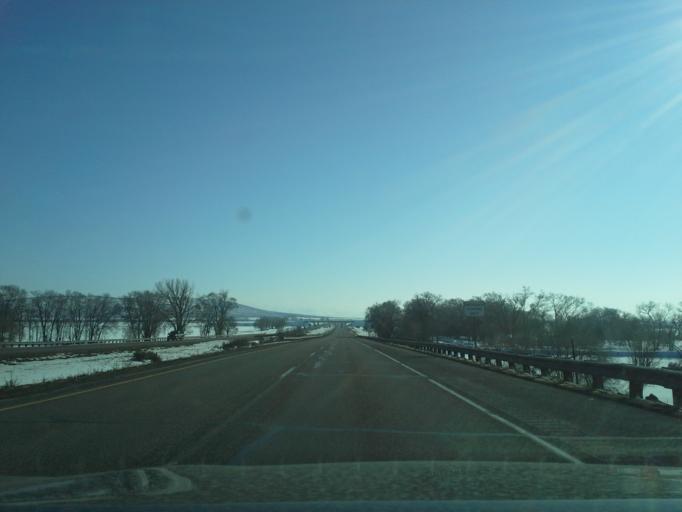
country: US
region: Idaho
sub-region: Bingham County
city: Blackfoot
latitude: 43.1472
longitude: -112.3889
